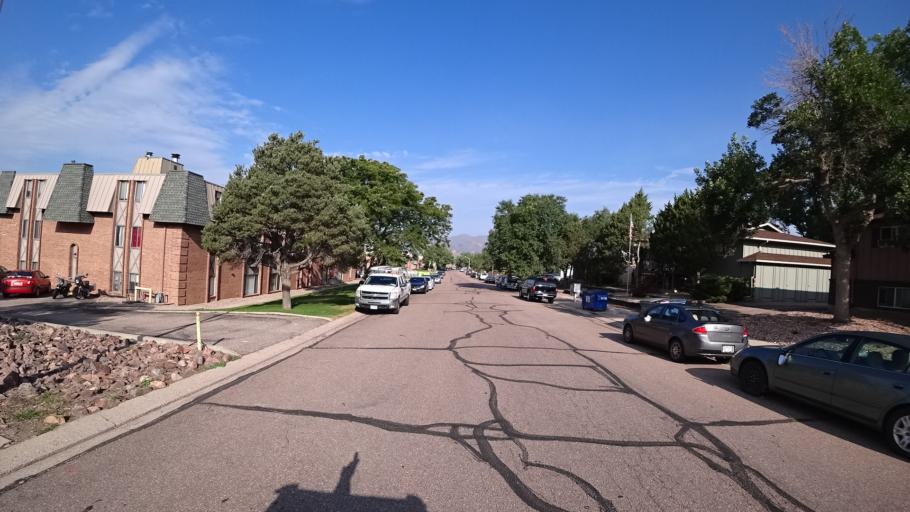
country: US
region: Colorado
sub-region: El Paso County
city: Colorado Springs
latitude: 38.8870
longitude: -104.8085
